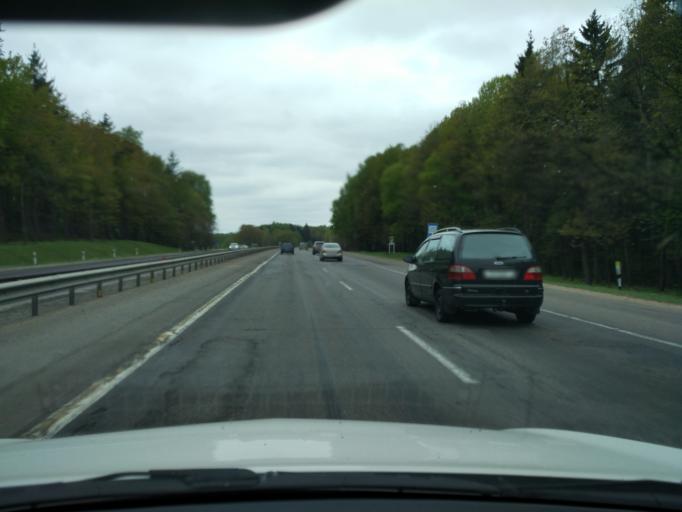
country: BY
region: Minsk
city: Zhdanovichy
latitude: 53.9082
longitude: 27.3765
